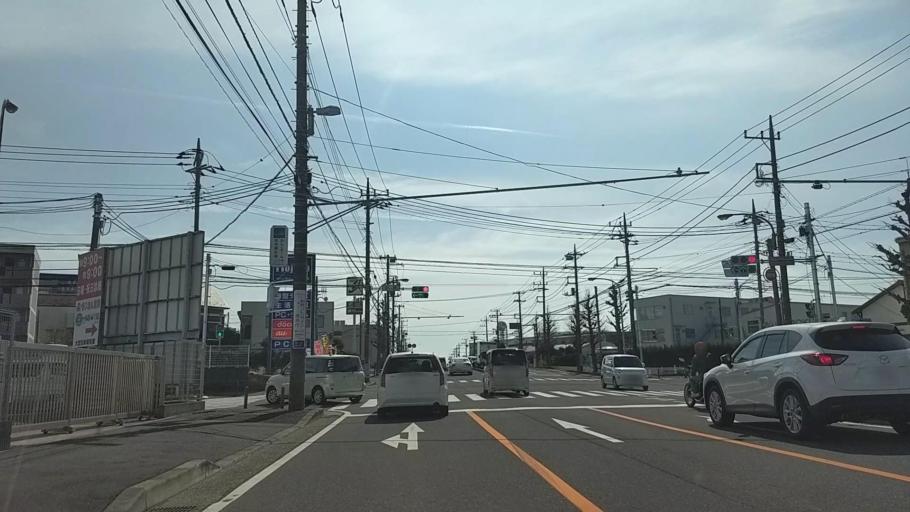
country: JP
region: Kanagawa
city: Fujisawa
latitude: 35.3899
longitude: 139.4575
